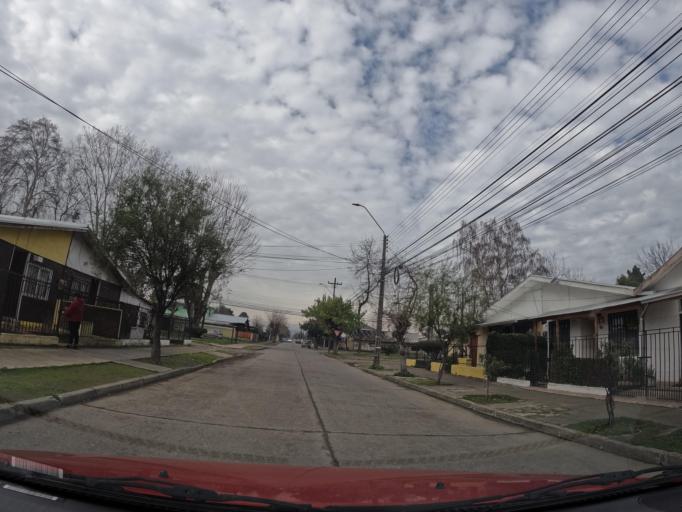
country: CL
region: Maule
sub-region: Provincia de Linares
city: Linares
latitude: -35.8535
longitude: -71.6029
